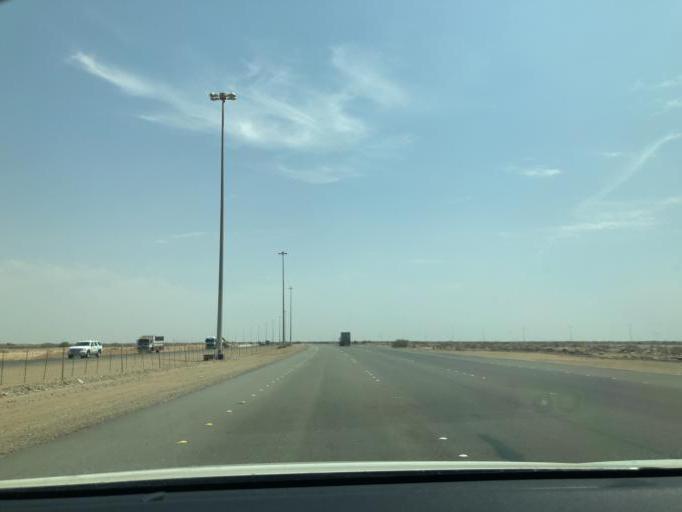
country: SA
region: Makkah
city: Rabigh
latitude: 22.2485
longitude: 39.1148
